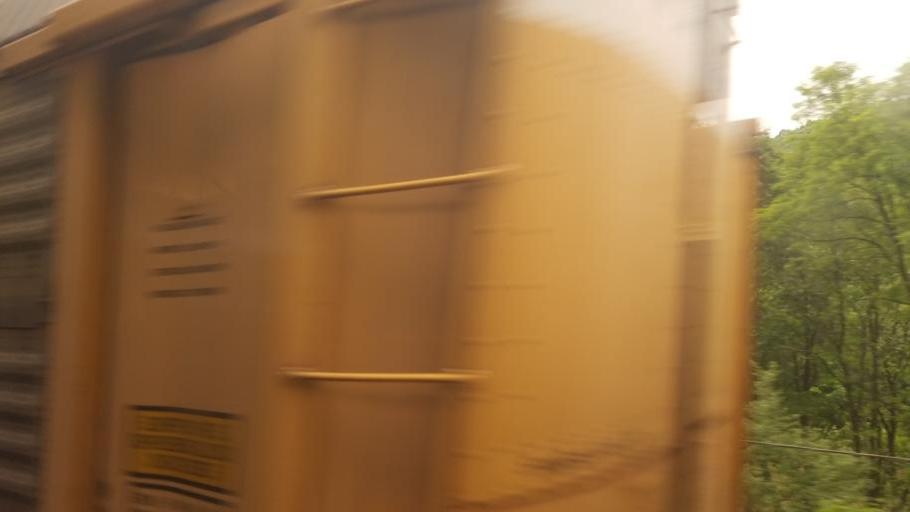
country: US
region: Pennsylvania
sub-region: Somerset County
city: Milford
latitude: 39.8768
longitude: -79.0883
